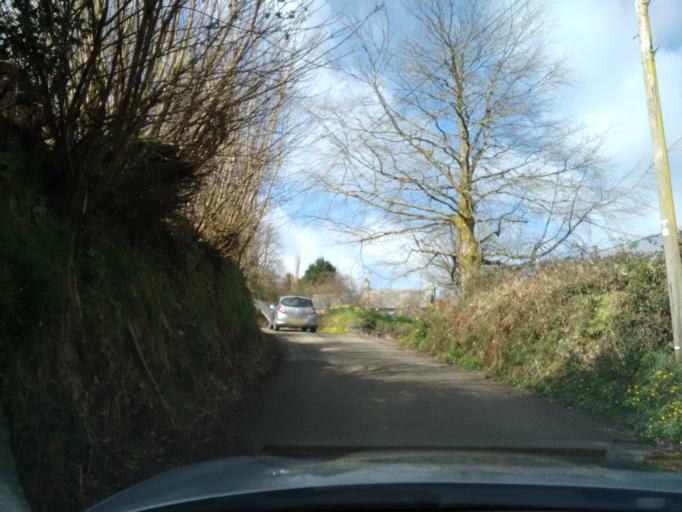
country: GB
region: England
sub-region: Cornwall
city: Launceston
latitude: 50.6004
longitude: -4.3416
